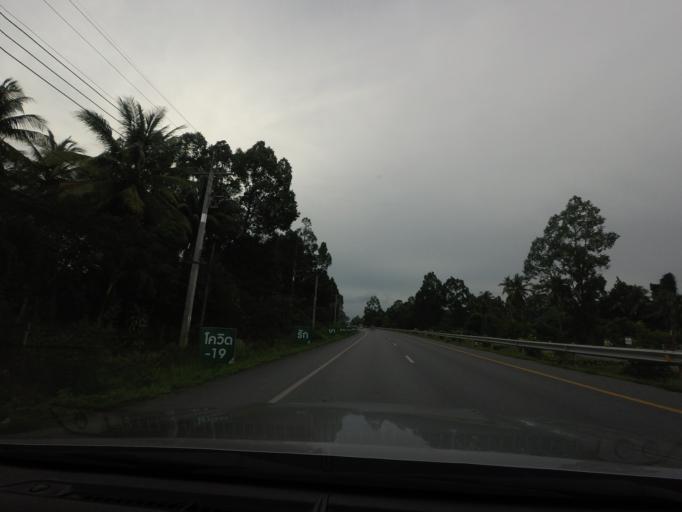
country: TH
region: Nakhon Si Thammarat
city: Chian Yai
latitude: 8.0990
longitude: 100.1106
